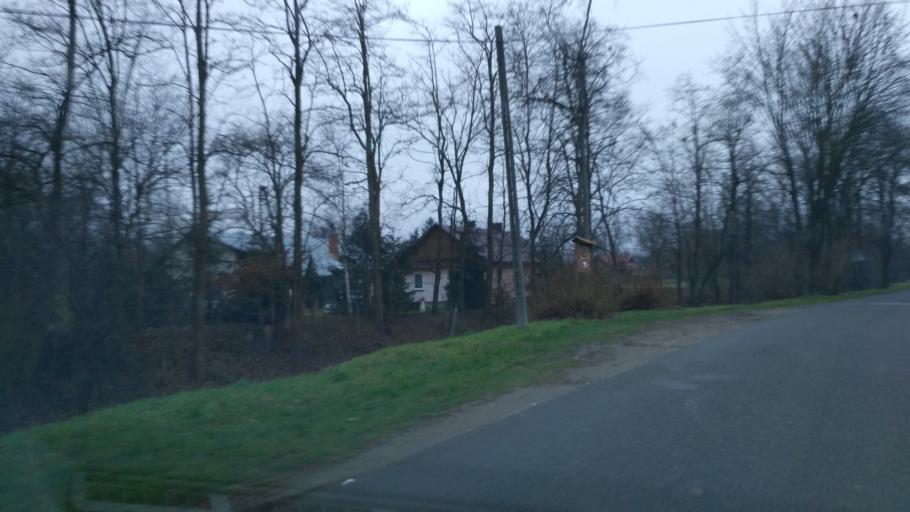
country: PL
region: Subcarpathian Voivodeship
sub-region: Powiat przeworski
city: Rozborz
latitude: 50.0536
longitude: 22.5467
